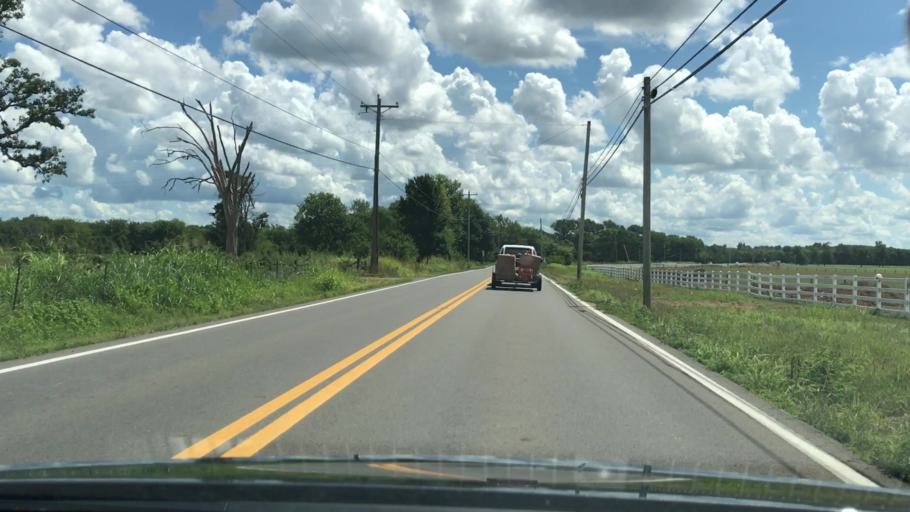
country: US
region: Tennessee
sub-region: Rutherford County
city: Murfreesboro
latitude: 35.8429
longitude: -86.5216
